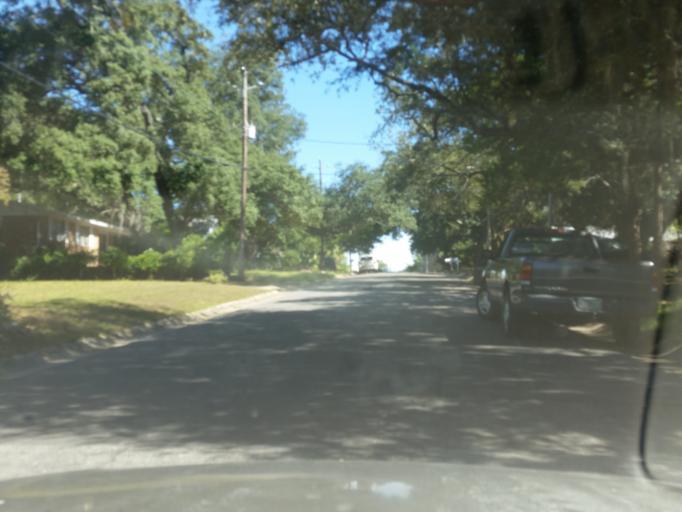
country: US
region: Florida
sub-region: Escambia County
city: East Pensacola Heights
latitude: 30.4264
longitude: -87.1849
